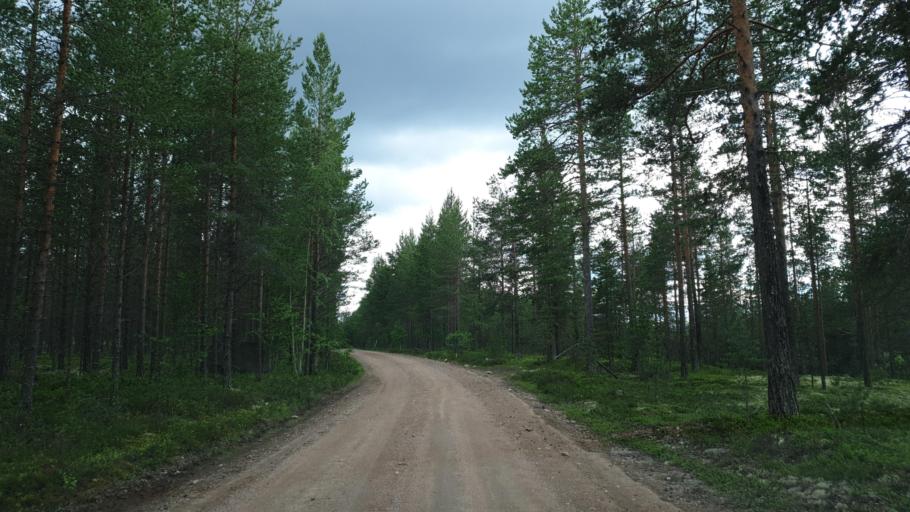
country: SE
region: Jaemtland
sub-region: Harjedalens Kommun
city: Sveg
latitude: 62.0392
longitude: 14.4965
